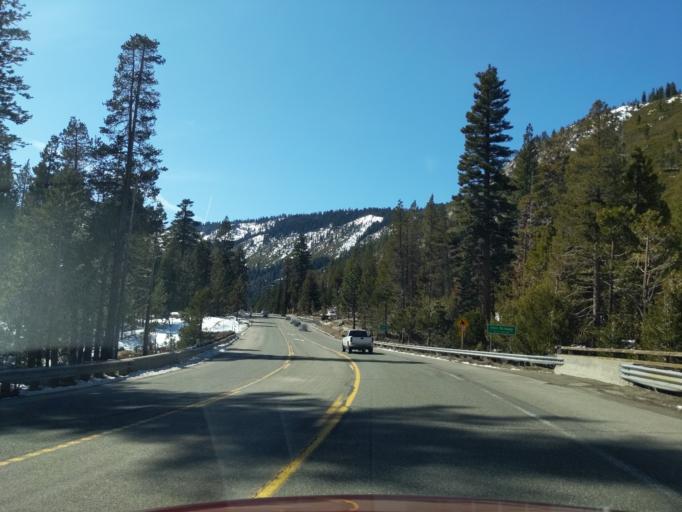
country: US
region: California
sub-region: El Dorado County
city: South Lake Tahoe
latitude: 38.8116
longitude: -120.1213
